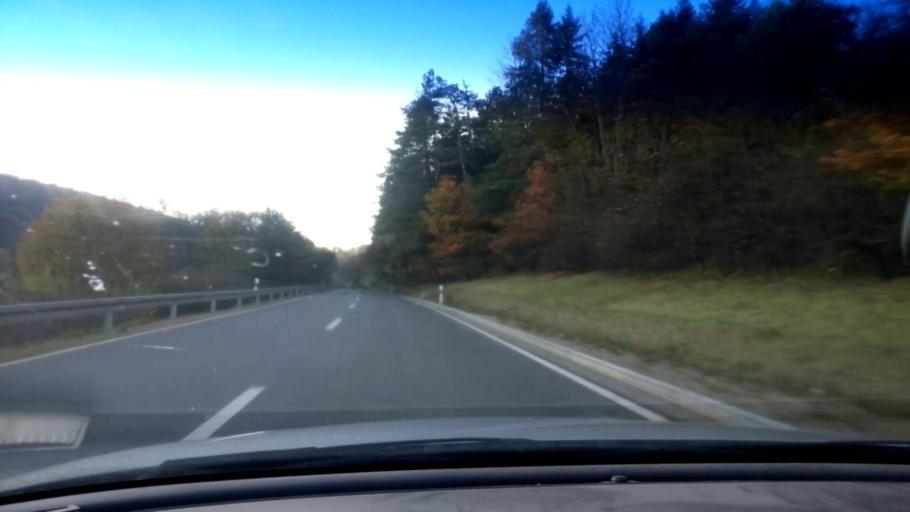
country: DE
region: Bavaria
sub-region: Upper Franconia
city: Heiligenstadt
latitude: 49.8494
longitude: 11.1872
